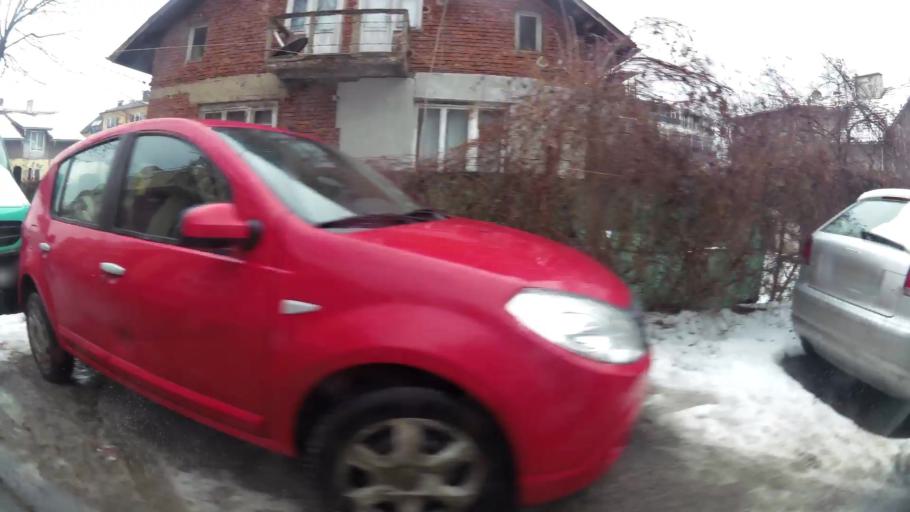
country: BG
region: Sofia-Capital
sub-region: Stolichna Obshtina
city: Sofia
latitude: 42.6603
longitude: 23.2675
